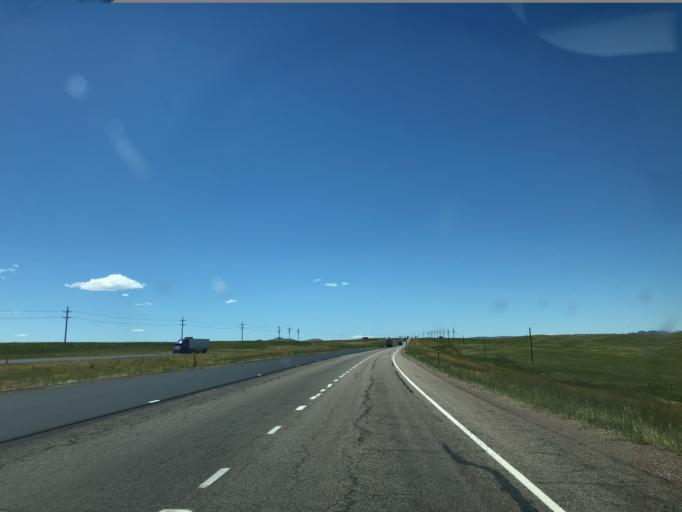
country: US
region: Wyoming
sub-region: Laramie County
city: Cheyenne
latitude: 41.1003
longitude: -105.0657
